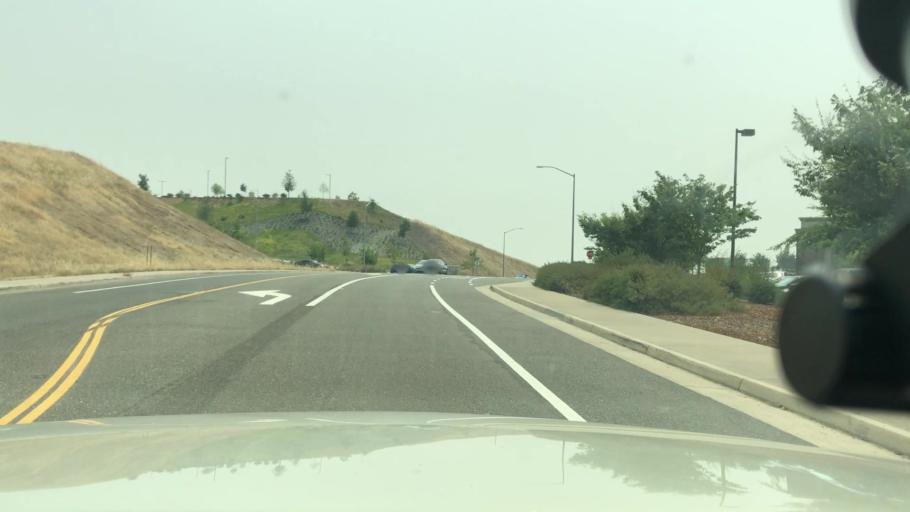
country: US
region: California
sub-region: El Dorado County
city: El Dorado Hills
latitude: 38.6468
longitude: -121.1070
